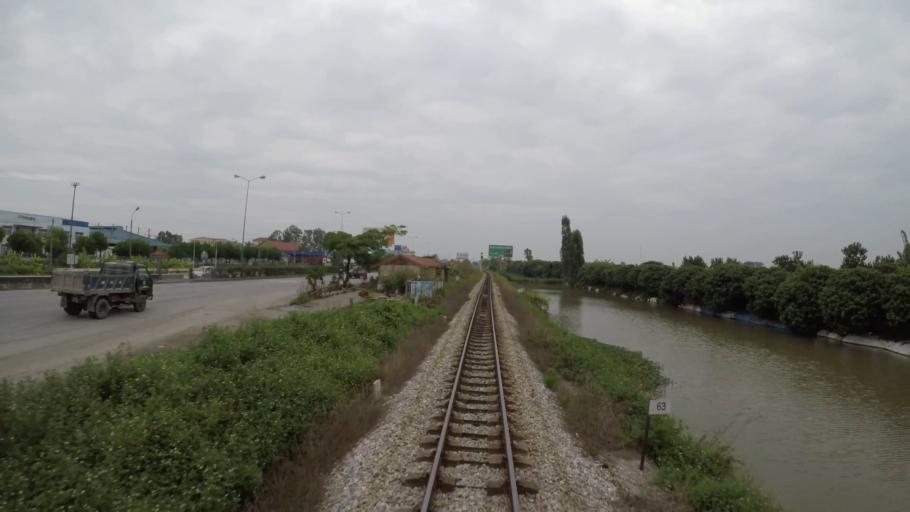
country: VN
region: Hai Duong
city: Nam Sach
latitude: 20.9701
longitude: 106.3817
